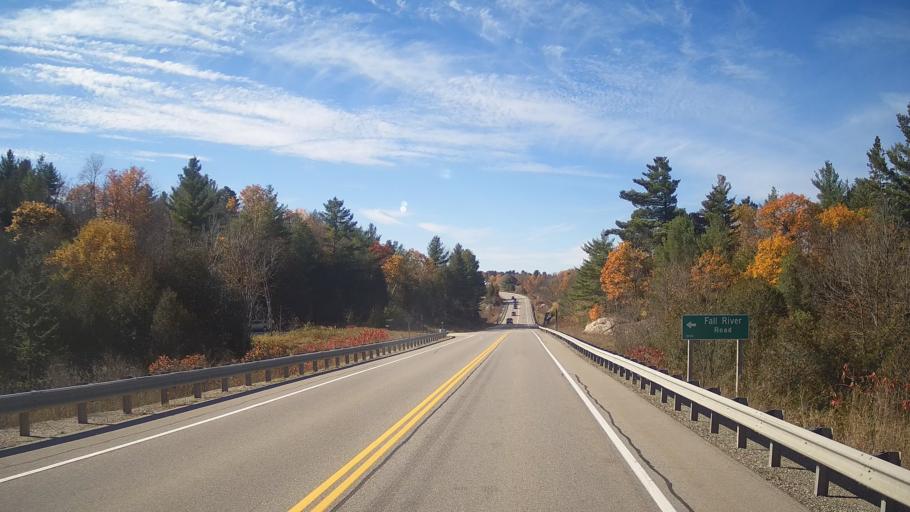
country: CA
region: Ontario
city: Perth
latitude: 44.8037
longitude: -76.6534
